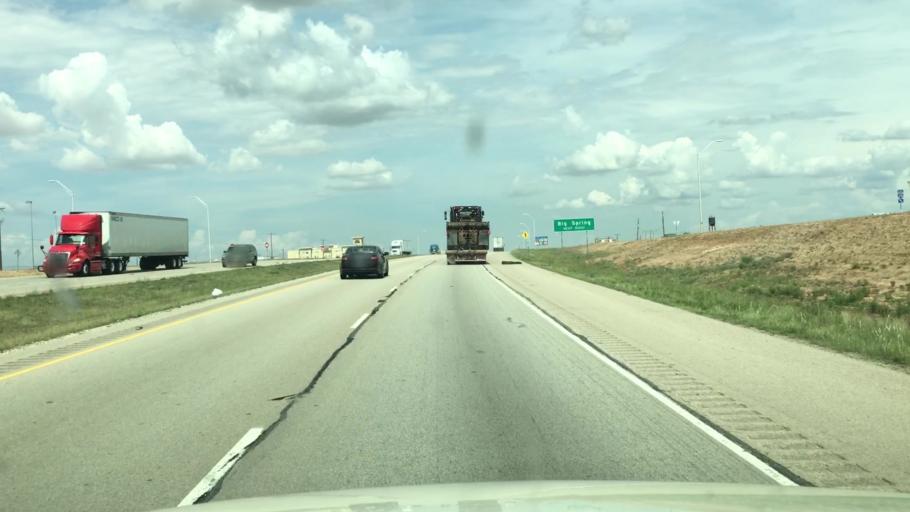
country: US
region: Texas
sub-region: Howard County
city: Big Spring
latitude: 32.2608
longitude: -101.5027
